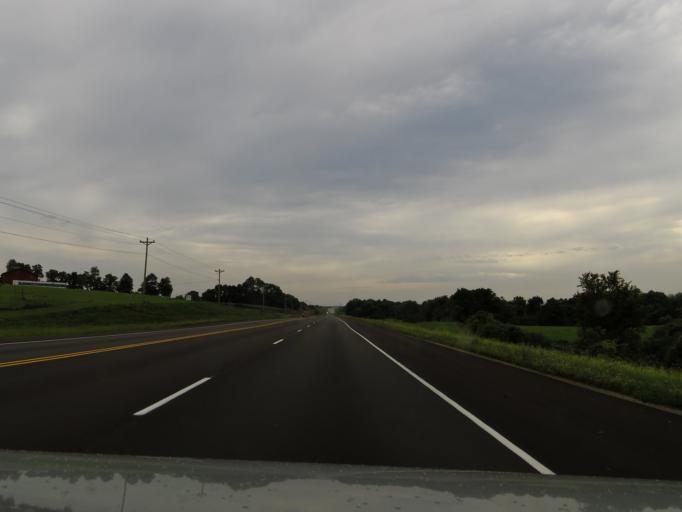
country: US
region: Ohio
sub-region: Brown County
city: Aberdeen
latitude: 38.6604
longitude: -83.8127
